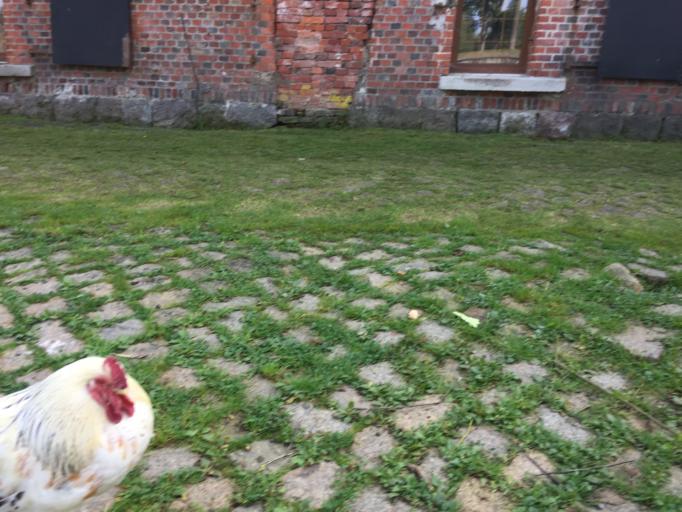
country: RU
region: Kaliningrad
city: Bol'shoe Isakovo
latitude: 54.6570
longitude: 20.5661
